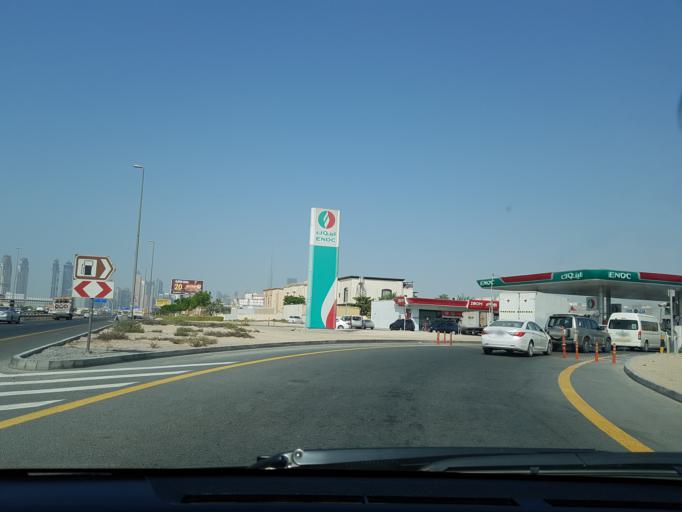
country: AE
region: Dubai
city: Dubai
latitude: 25.1524
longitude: 55.2621
